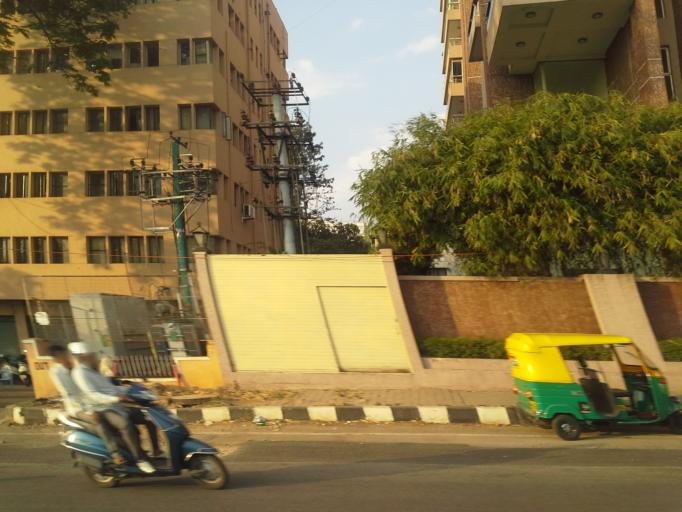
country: IN
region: Karnataka
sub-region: Bangalore Urban
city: Bangalore
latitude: 12.9839
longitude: 77.5803
